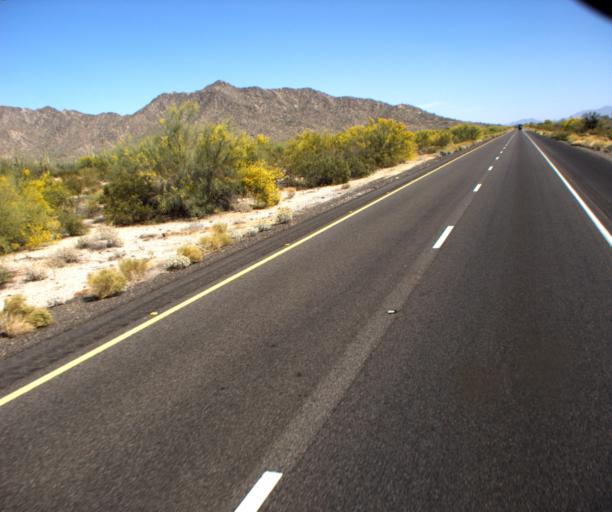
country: US
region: Arizona
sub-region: Maricopa County
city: Gila Bend
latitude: 32.8686
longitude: -112.4273
